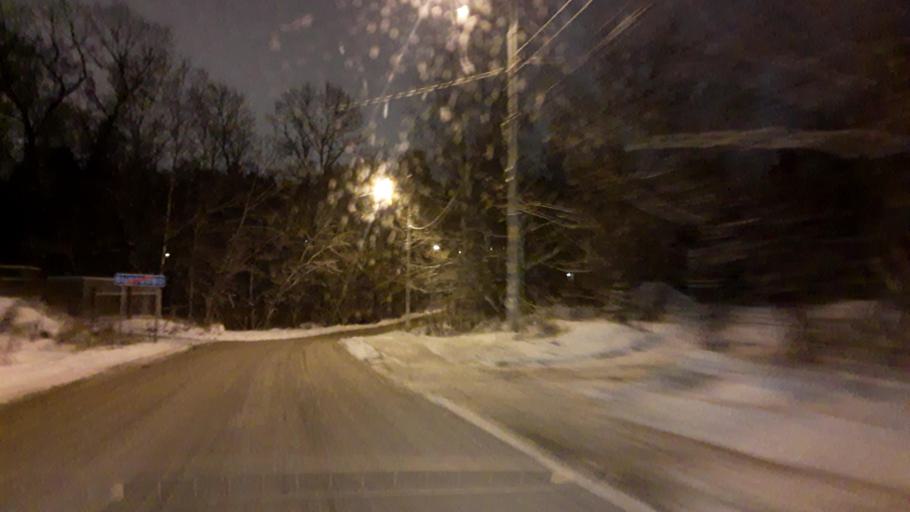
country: RU
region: Moskovskaya
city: Biryulevo Zapadnoye
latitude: 55.5696
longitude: 37.6256
